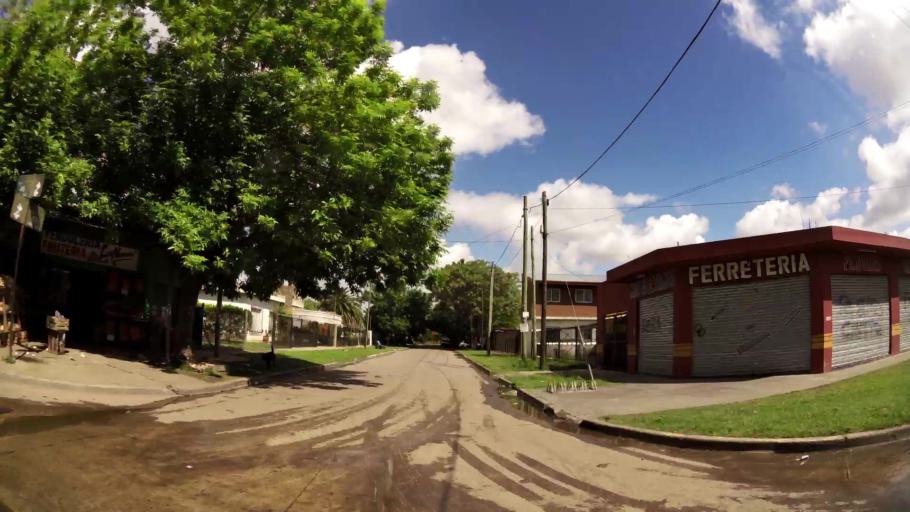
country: AR
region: Buenos Aires
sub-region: Partido de Quilmes
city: Quilmes
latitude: -34.8340
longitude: -58.1814
